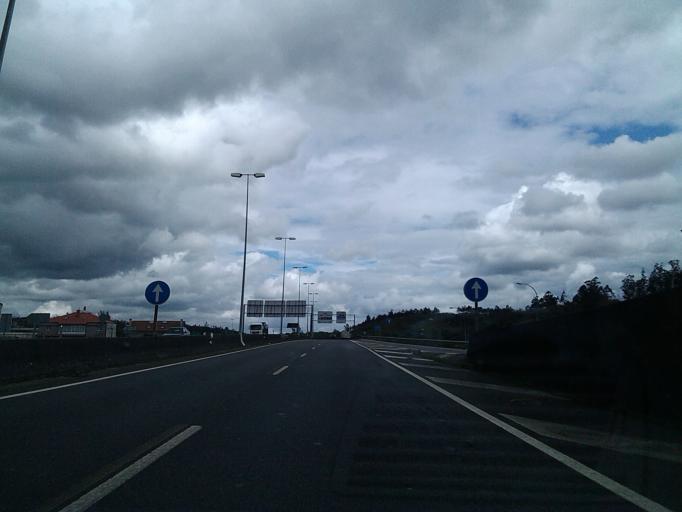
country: ES
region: Galicia
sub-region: Provincia da Coruna
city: Santiago de Compostela
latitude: 42.8911
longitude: -8.5080
